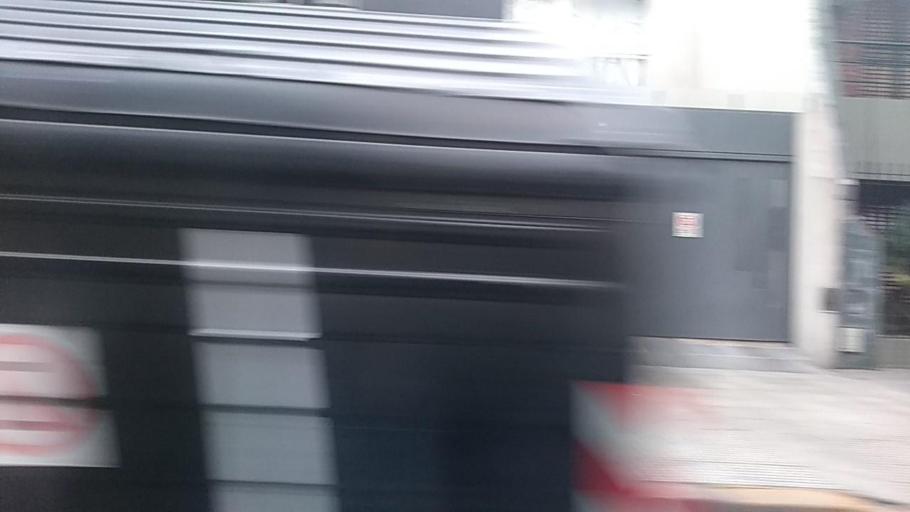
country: AR
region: Buenos Aires F.D.
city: Villa Santa Rita
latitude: -34.6052
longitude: -58.5066
